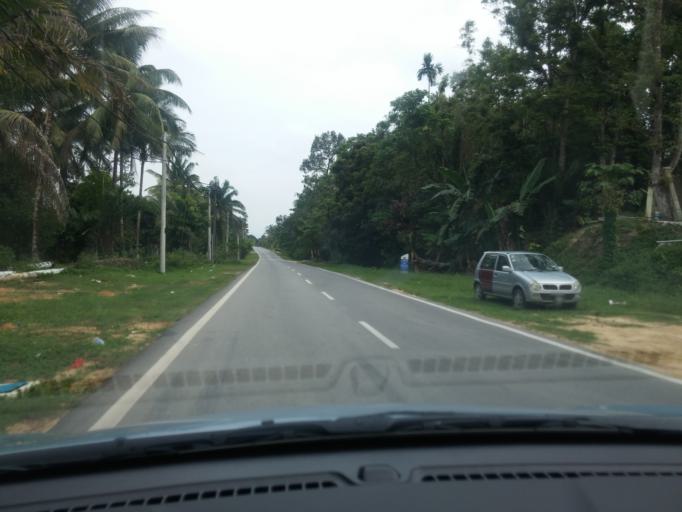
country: MY
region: Pahang
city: Kuantan
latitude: 3.8415
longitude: 103.1612
